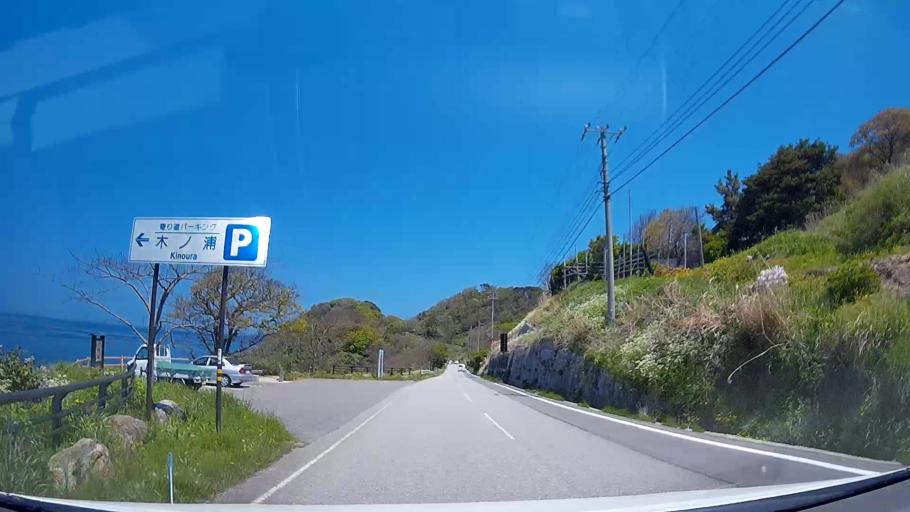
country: JP
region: Ishikawa
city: Nanao
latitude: 37.5290
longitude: 137.2718
